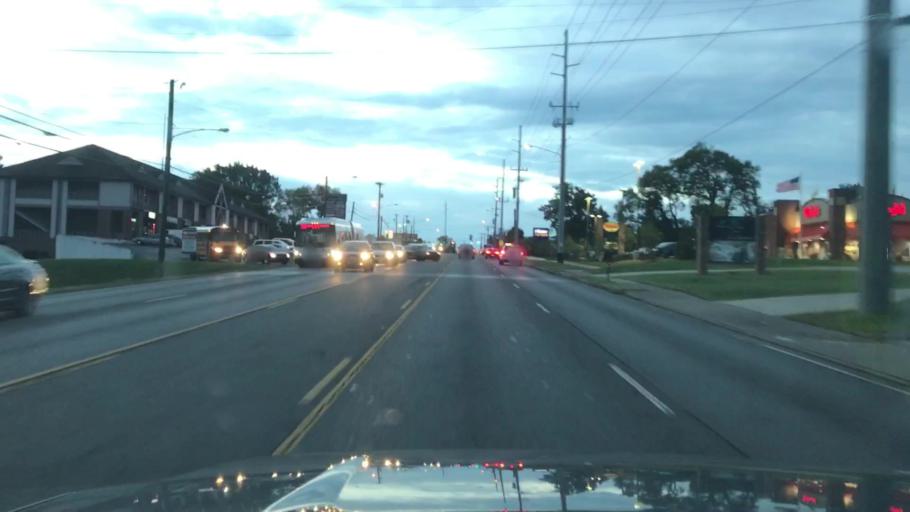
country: US
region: Tennessee
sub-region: Rutherford County
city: La Vergne
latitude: 36.0917
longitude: -86.6515
